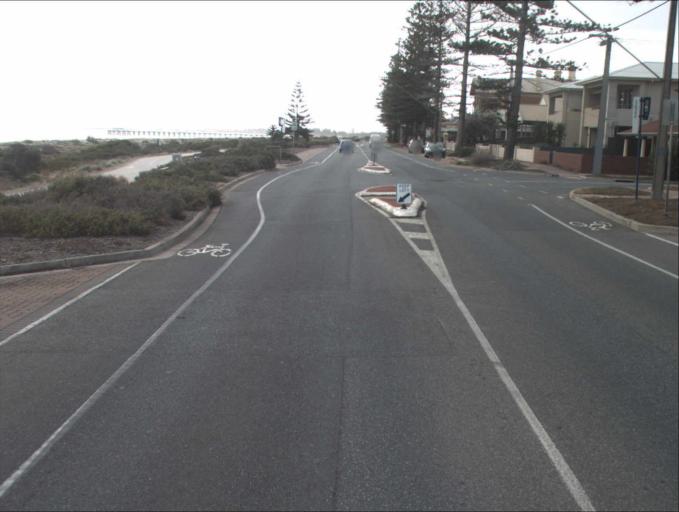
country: AU
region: South Australia
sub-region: Port Adelaide Enfield
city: Birkenhead
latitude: -34.8327
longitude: 138.4826
